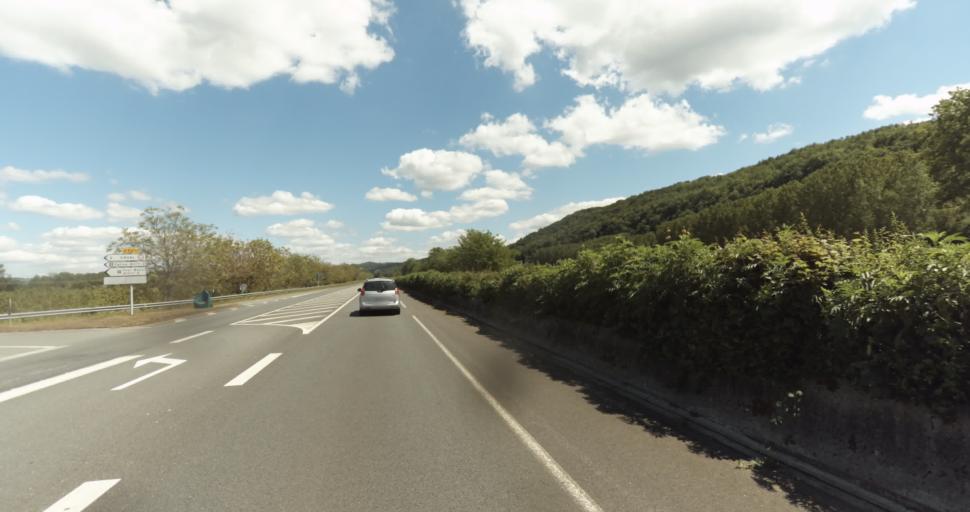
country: FR
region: Aquitaine
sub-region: Departement de la Dordogne
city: Belves
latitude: 44.8261
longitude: 0.9514
